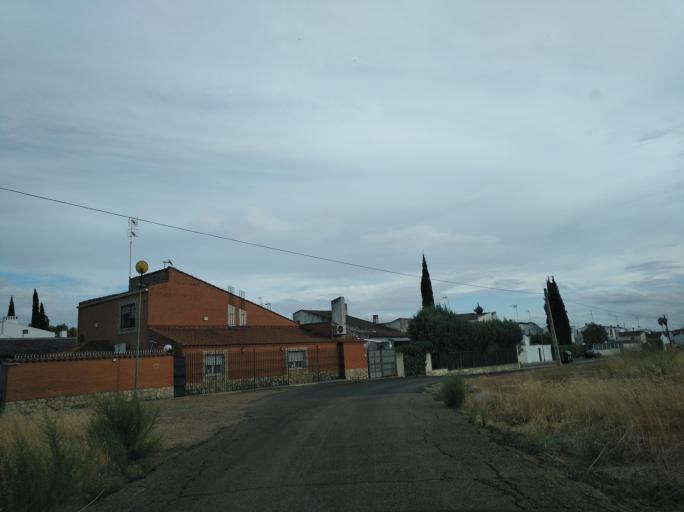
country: ES
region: Extremadura
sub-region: Provincia de Badajoz
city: Badajoz
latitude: 38.8860
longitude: -7.0139
